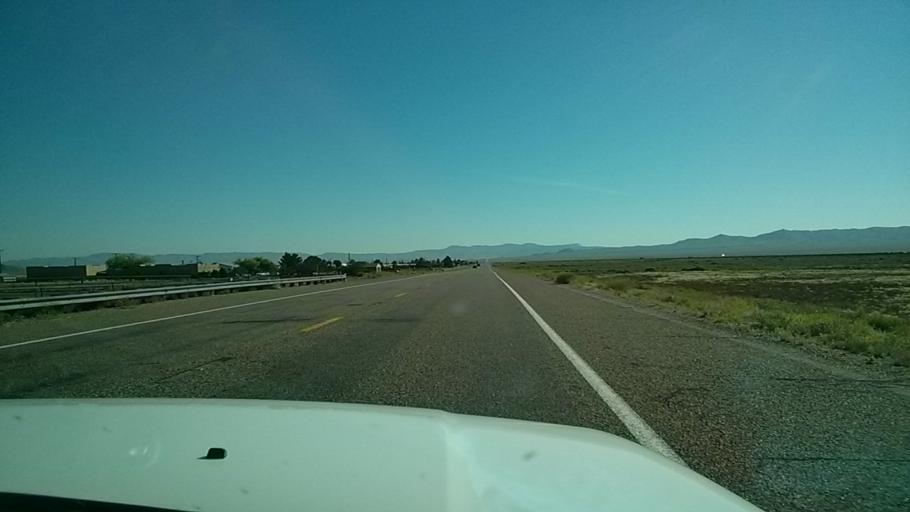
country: US
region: Arizona
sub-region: Mohave County
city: New Kingman-Butler
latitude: 35.2956
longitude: -113.9358
